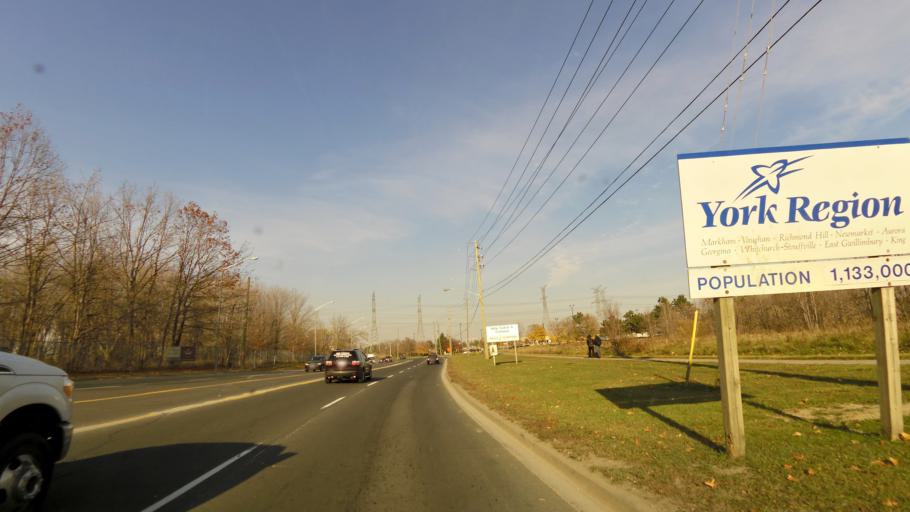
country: CA
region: Ontario
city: Concord
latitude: 43.7766
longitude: -79.5215
